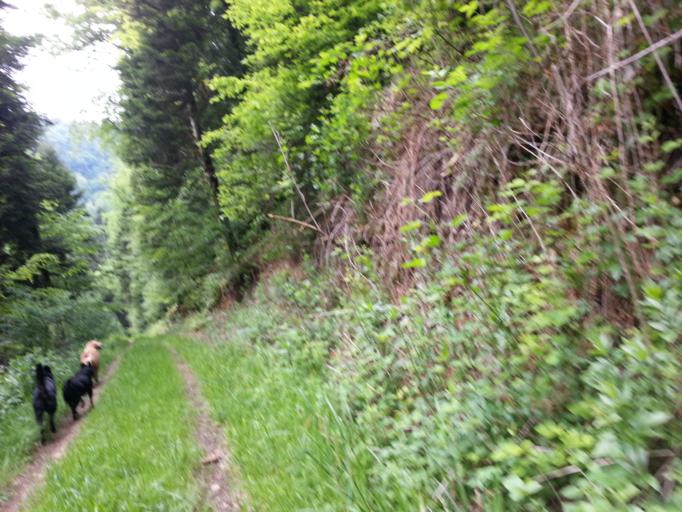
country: FR
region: Franche-Comte
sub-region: Departement du Jura
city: Salins-les-Bains
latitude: 47.0027
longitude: 5.9845
